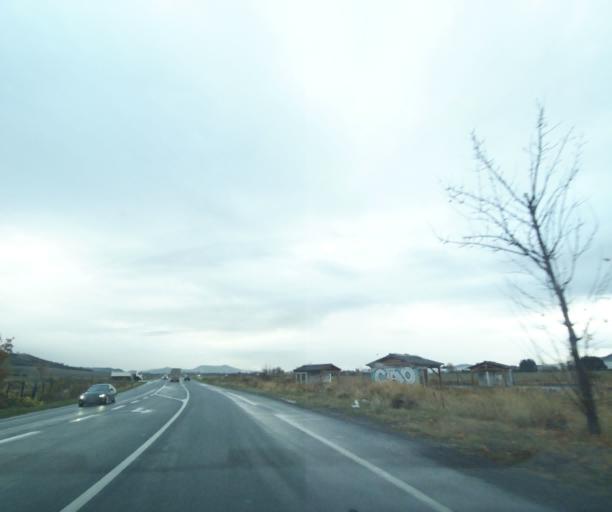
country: FR
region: Auvergne
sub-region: Departement du Puy-de-Dome
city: Perignat-les-Sarlieve
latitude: 45.7618
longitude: 3.1506
